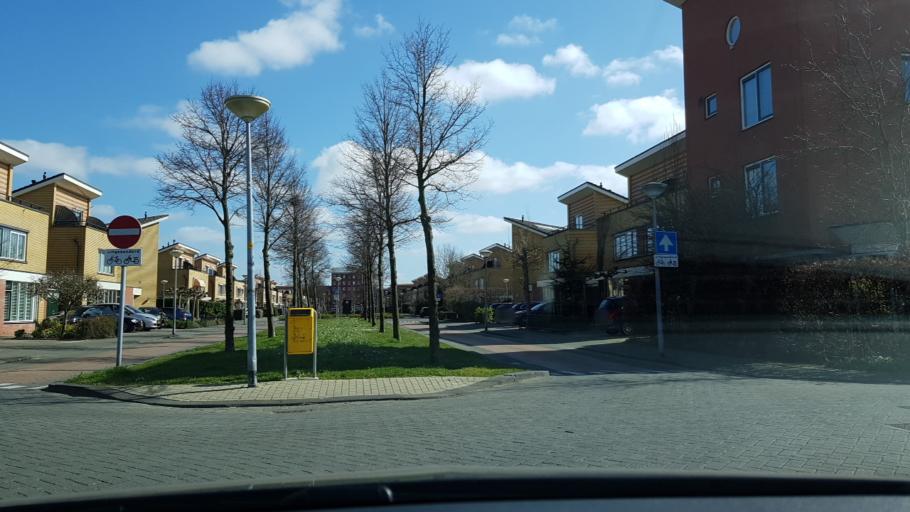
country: NL
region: South Holland
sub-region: Gemeente Hillegom
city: Hillegom
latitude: 52.2721
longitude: 4.6070
